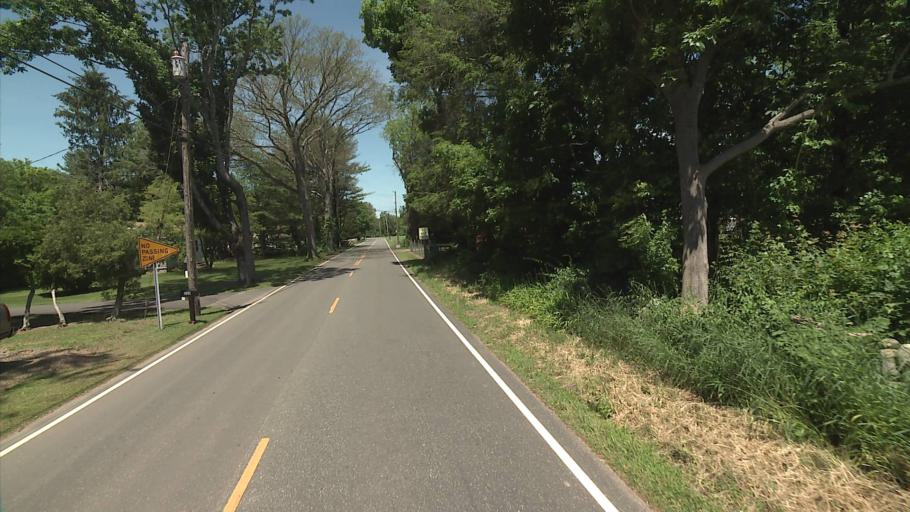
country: US
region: Rhode Island
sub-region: Washington County
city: Hopkinton
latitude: 41.4475
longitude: -71.8059
